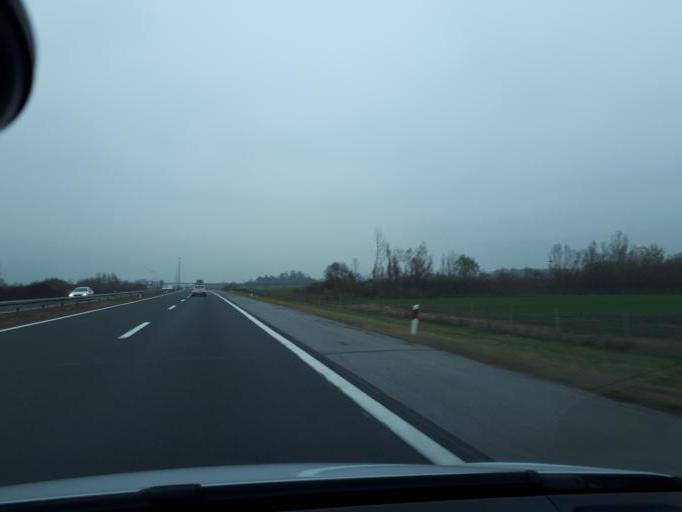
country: HR
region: Brodsko-Posavska
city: Resetari
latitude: 45.2178
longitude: 17.5075
